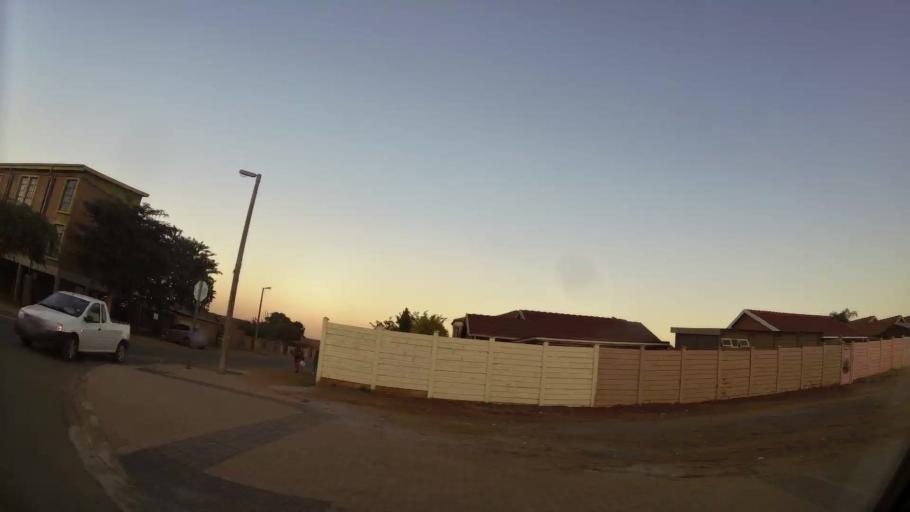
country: ZA
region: North-West
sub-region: Bojanala Platinum District Municipality
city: Rustenburg
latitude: -25.6493
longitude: 27.2062
